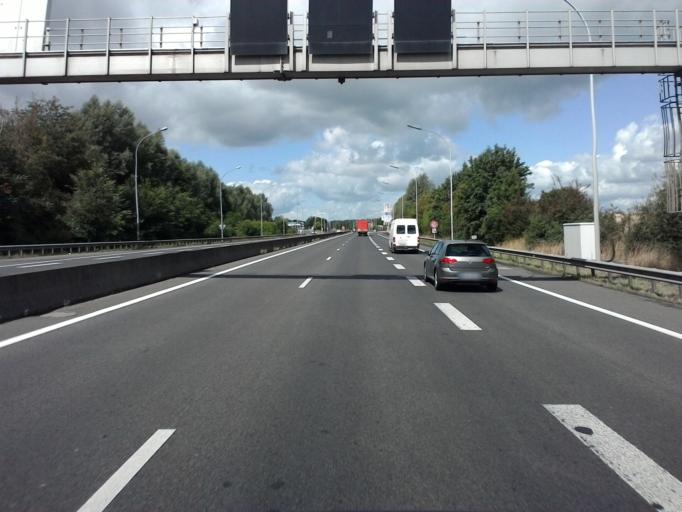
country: LU
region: Luxembourg
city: Capellen
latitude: 49.6350
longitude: 5.9786
